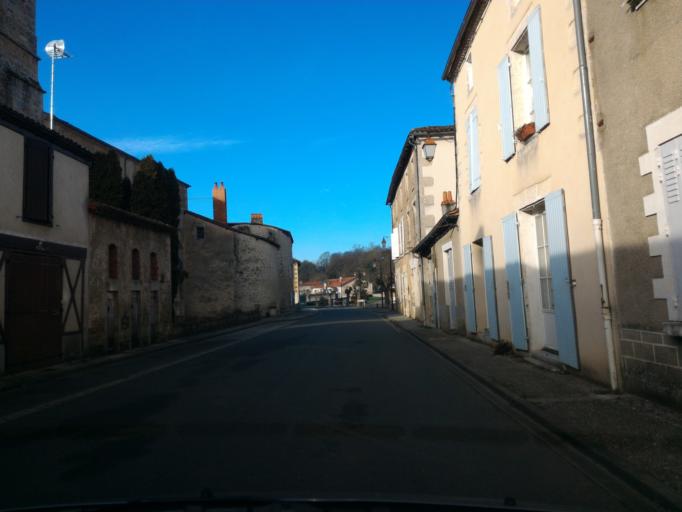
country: FR
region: Poitou-Charentes
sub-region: Departement de la Charente
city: Champagne-Mouton
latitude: 46.0258
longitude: 0.5167
